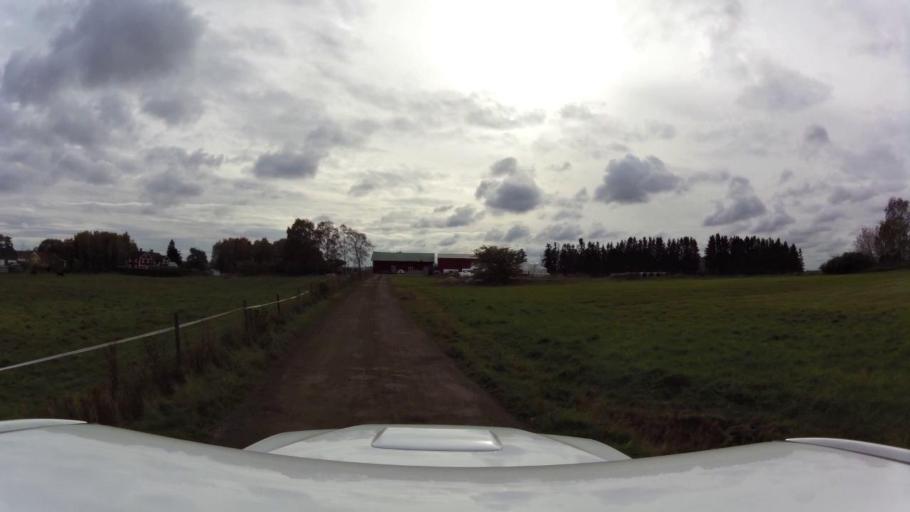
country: SE
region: OEstergoetland
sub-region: Linkopings Kommun
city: Ekangen
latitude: 58.4495
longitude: 15.5846
